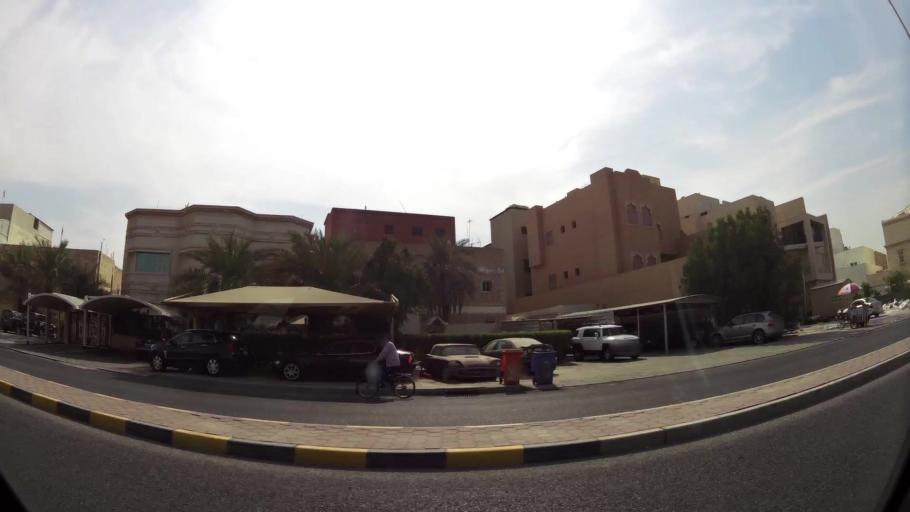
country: KW
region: Al Asimah
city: Ash Shamiyah
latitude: 29.3380
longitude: 47.9556
